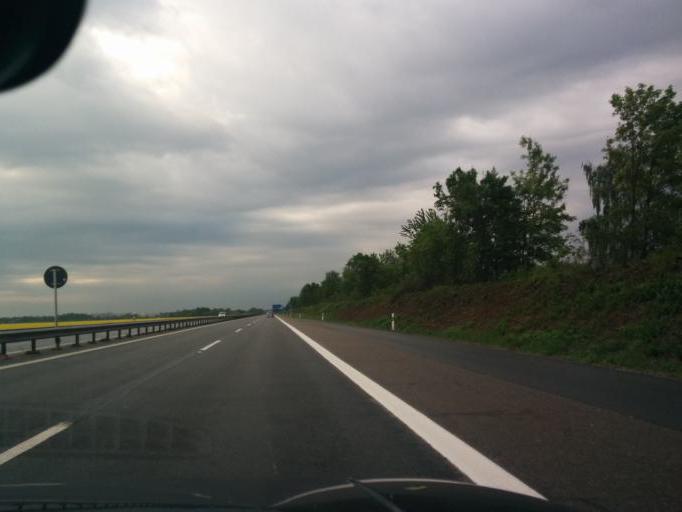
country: DE
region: Bavaria
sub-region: Upper Bavaria
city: Unterhaching
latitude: 48.0659
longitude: 11.6327
